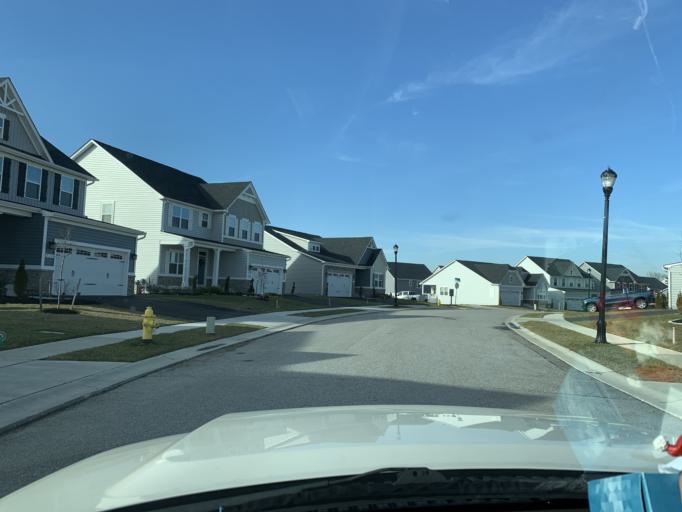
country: US
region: Maryland
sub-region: Anne Arundel County
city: Fort Meade
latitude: 39.1374
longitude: -76.7394
